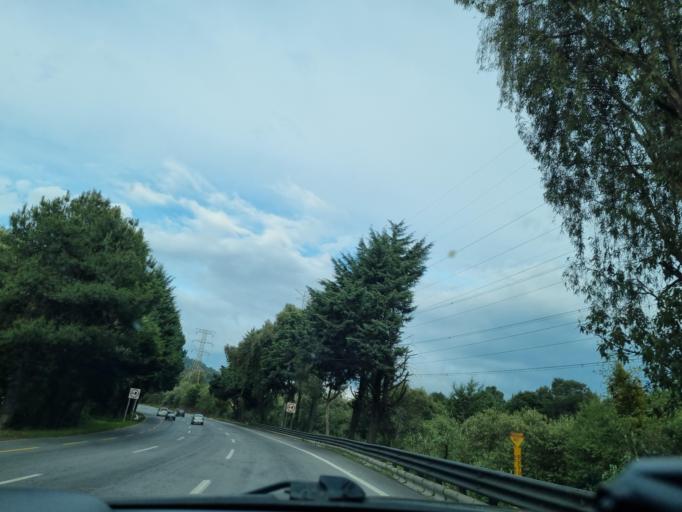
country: MX
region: Morelos
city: San Jeronimo Acazulco
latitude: 19.2885
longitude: -99.4332
